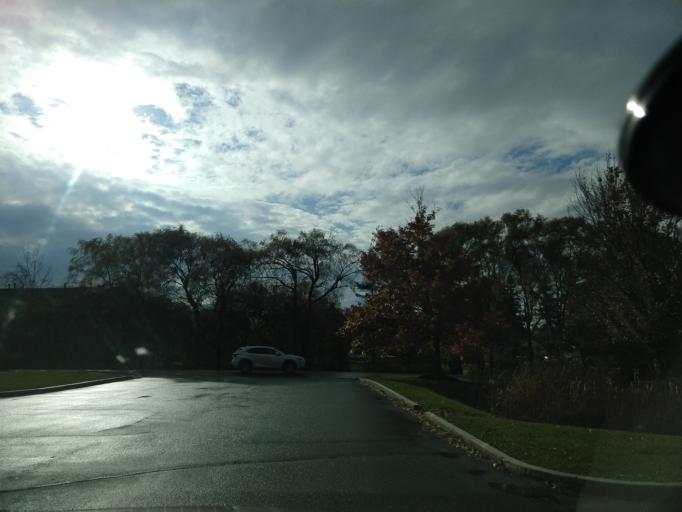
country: US
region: New York
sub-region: Tompkins County
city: Lansing
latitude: 42.4786
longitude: -76.4792
